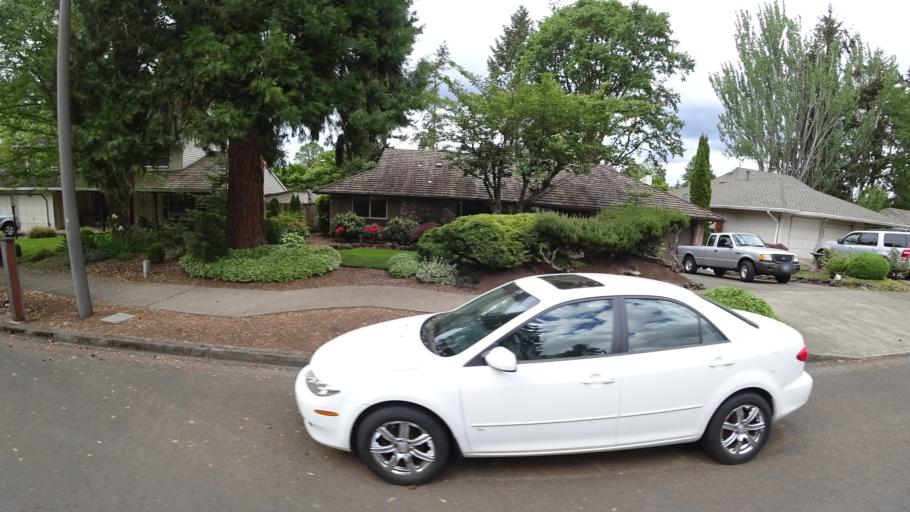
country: US
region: Oregon
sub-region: Washington County
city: Beaverton
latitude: 45.4776
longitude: -122.8276
